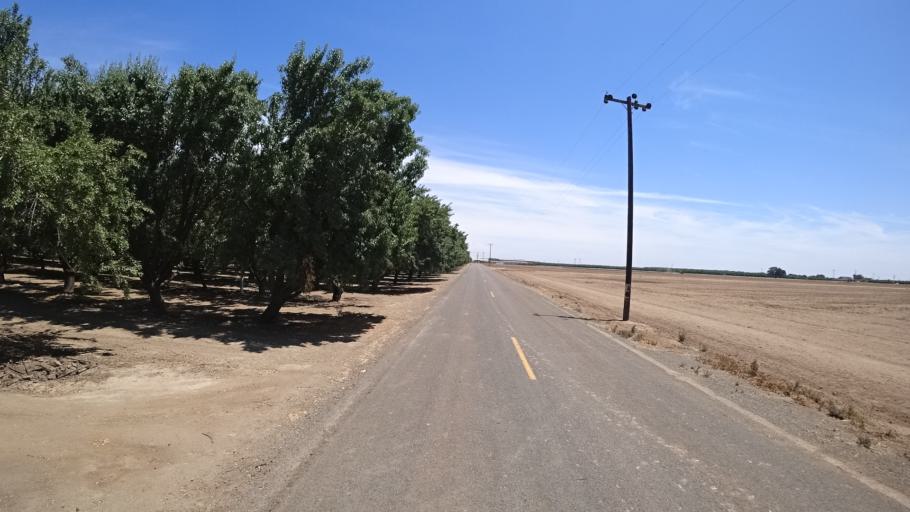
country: US
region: California
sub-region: Kings County
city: Armona
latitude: 36.3390
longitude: -119.7484
